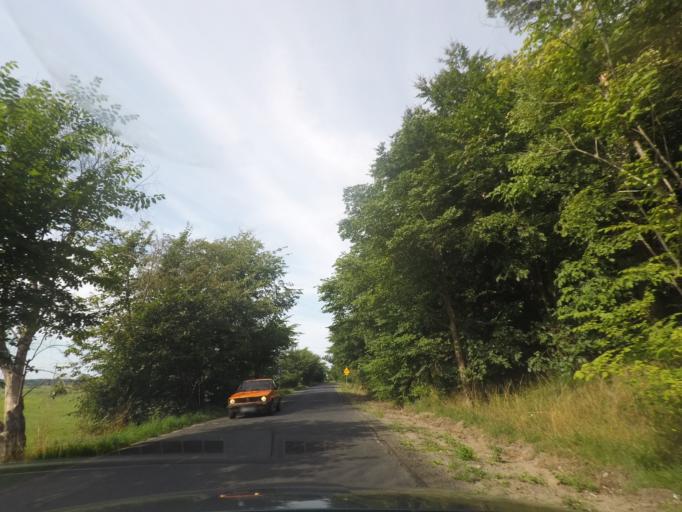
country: PL
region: Pomeranian Voivodeship
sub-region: Powiat slupski
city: Smoldzino
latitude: 54.6505
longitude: 17.1889
